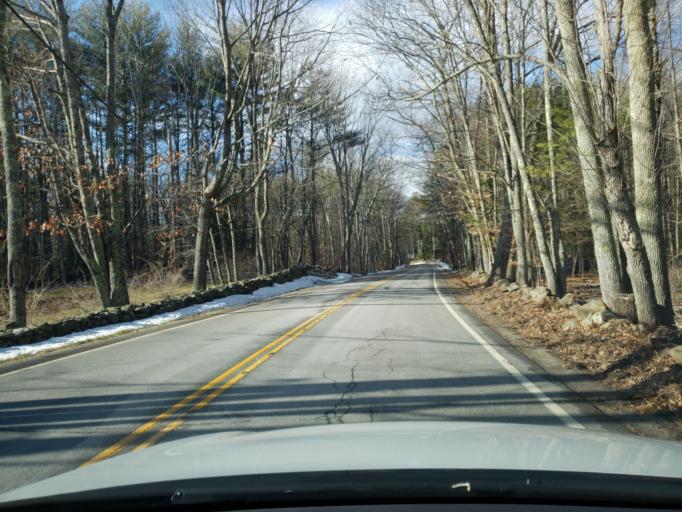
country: US
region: New Hampshire
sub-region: Hillsborough County
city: Lyndeborough
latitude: 42.9849
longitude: -71.7936
